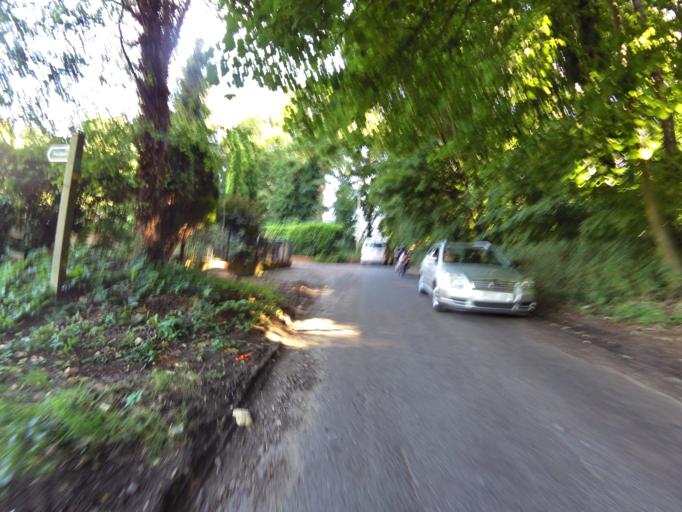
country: GB
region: England
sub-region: Suffolk
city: Kesgrave
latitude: 52.0427
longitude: 1.2533
